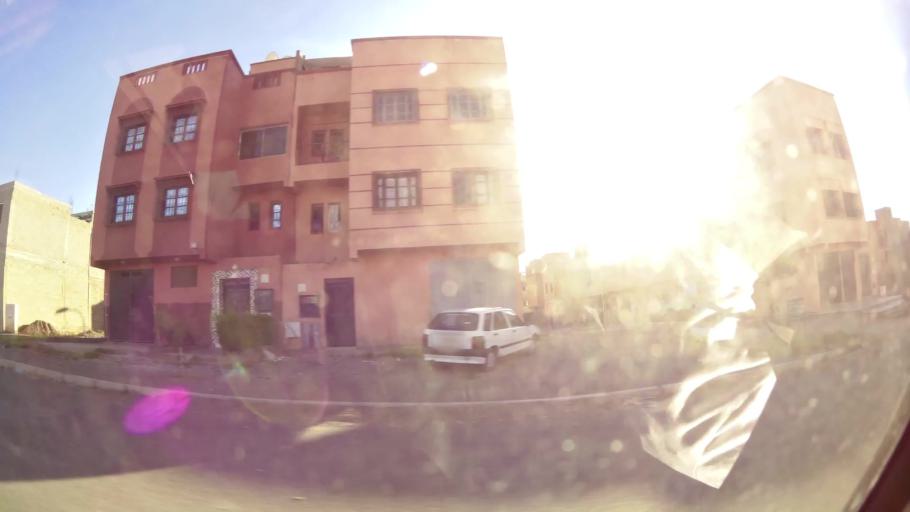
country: MA
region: Marrakech-Tensift-Al Haouz
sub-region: Marrakech
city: Marrakesh
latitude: 31.7588
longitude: -8.1003
